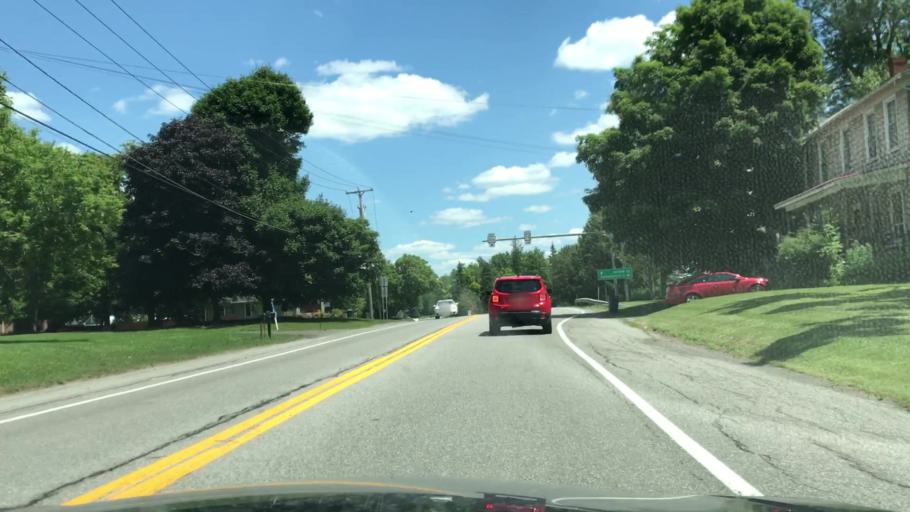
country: US
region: New York
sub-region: Erie County
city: East Aurora
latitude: 42.7679
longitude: -78.5513
